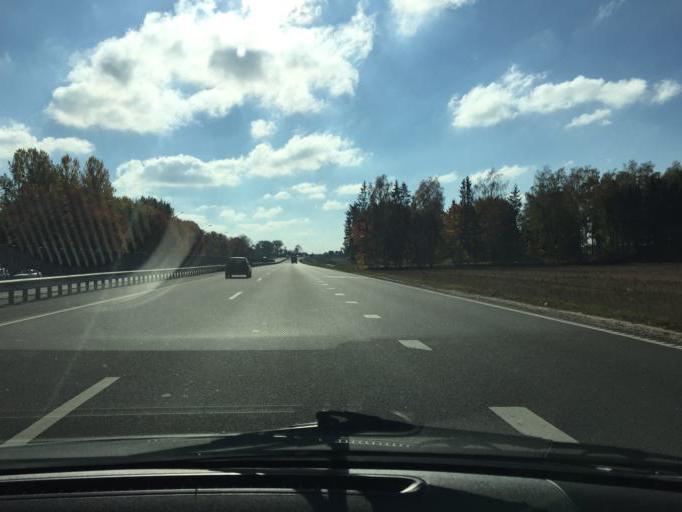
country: BY
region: Minsk
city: Slutsk
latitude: 53.0904
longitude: 27.5698
